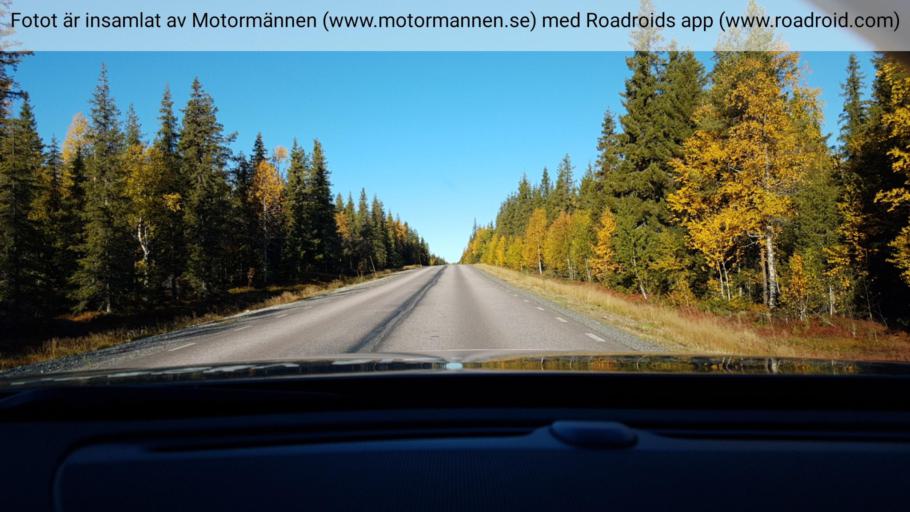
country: SE
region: Vaesterbotten
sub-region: Skelleftea Kommun
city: Storvik
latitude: 65.3534
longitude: 20.4805
